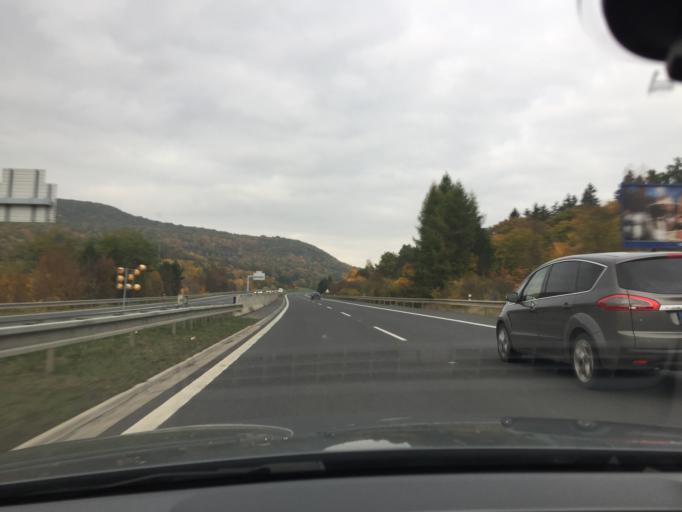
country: CZ
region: Ustecky
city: Rehlovice
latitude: 50.6167
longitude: 13.9709
